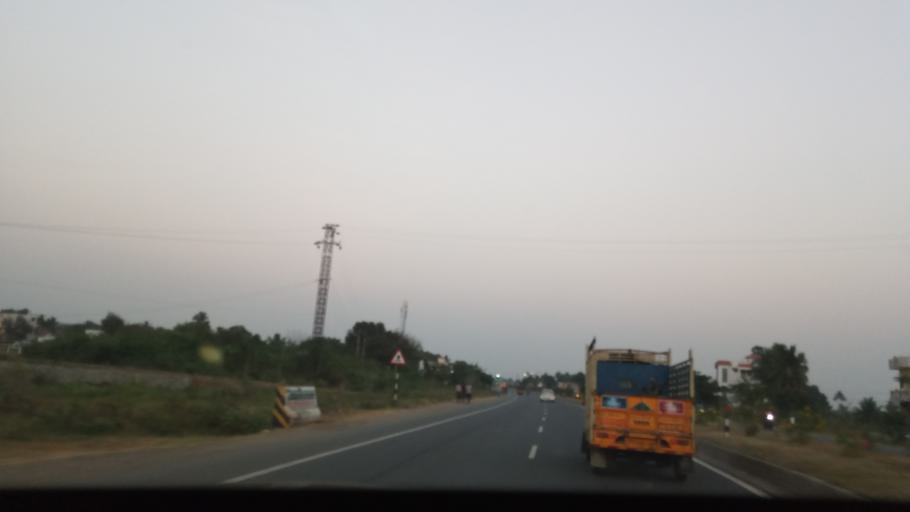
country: IN
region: Tamil Nadu
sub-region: Salem
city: Belur
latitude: 11.6531
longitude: 78.3713
